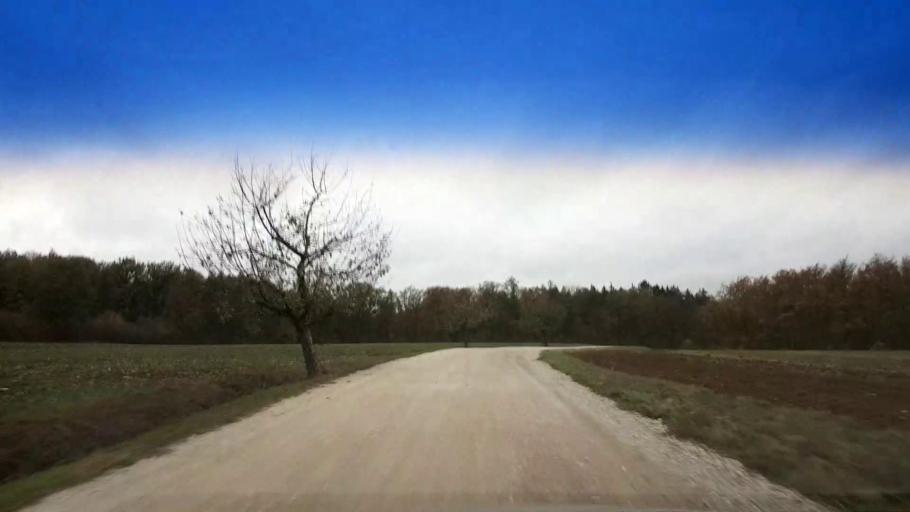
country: DE
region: Bavaria
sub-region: Upper Franconia
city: Schesslitz
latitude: 49.9663
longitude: 11.0319
